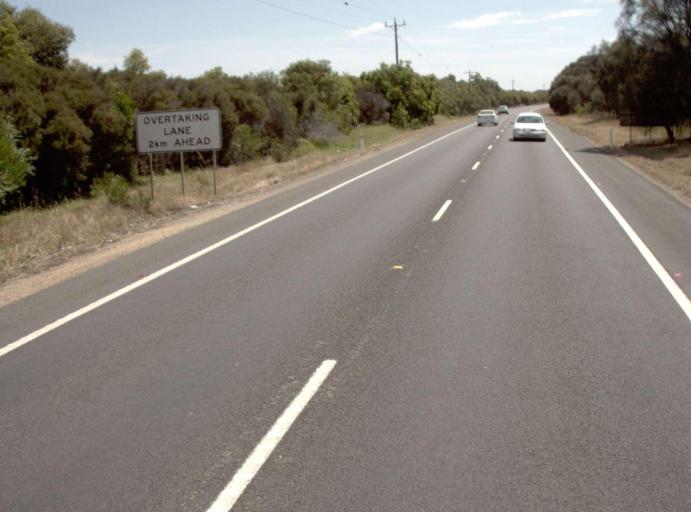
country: AU
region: Victoria
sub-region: Wellington
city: Sale
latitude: -38.0992
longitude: 146.9733
